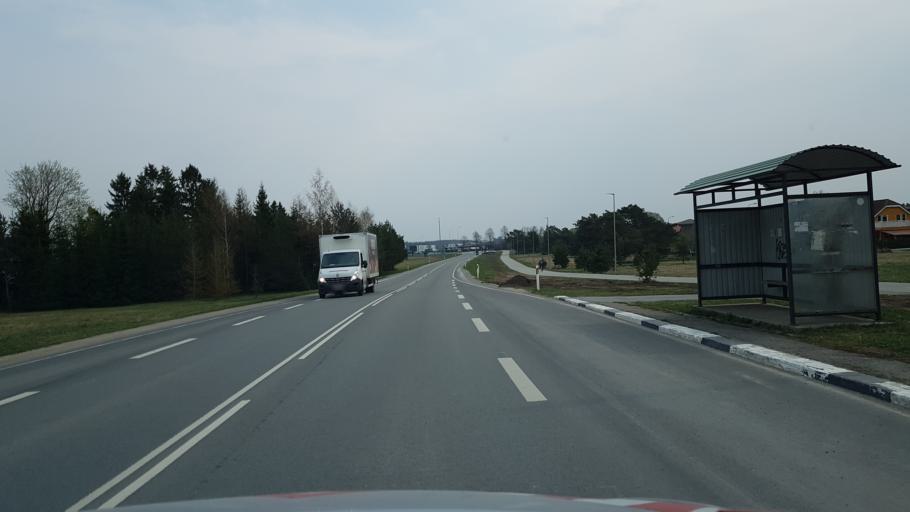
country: EE
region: Harju
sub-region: Tallinna linn
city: Tallinn
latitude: 59.3859
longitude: 24.8158
